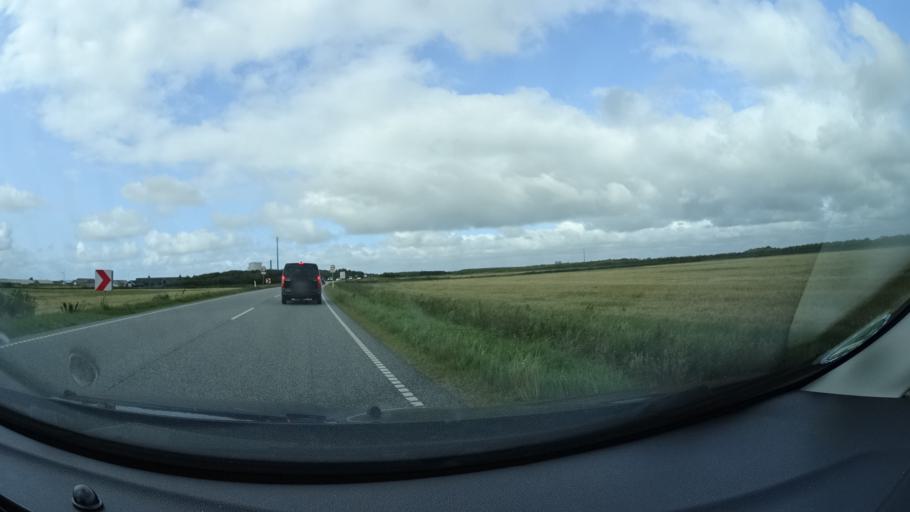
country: DK
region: Central Jutland
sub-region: Lemvig Kommune
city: Harboore
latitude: 56.6061
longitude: 8.1827
